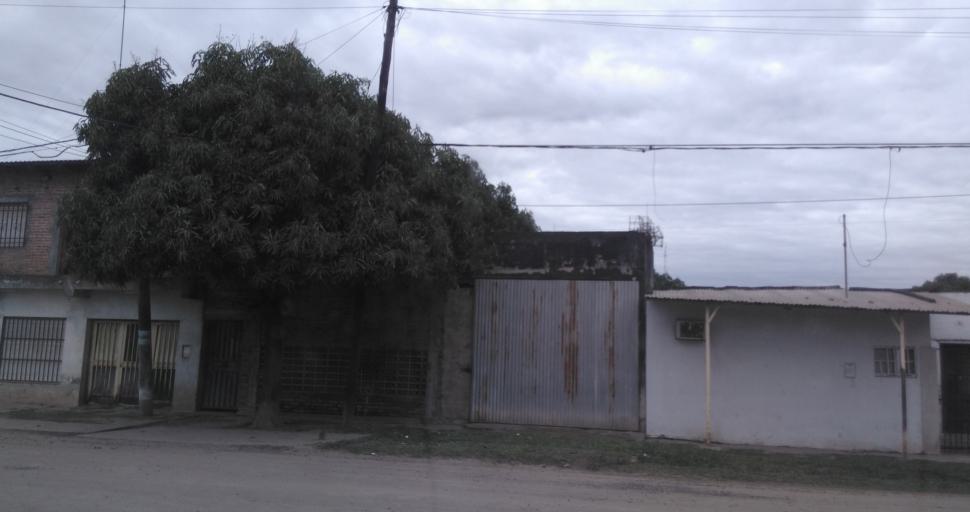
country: AR
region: Chaco
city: Resistencia
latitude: -27.4695
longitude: -58.9693
